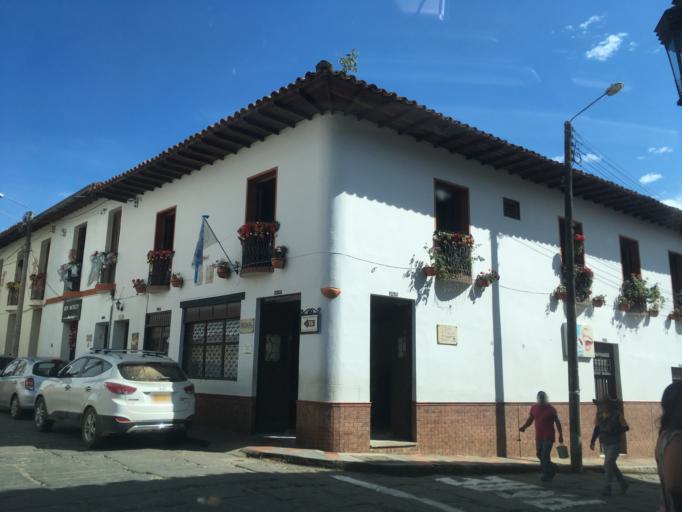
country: CO
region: Santander
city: Coromoro
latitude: 6.2877
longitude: -73.1480
